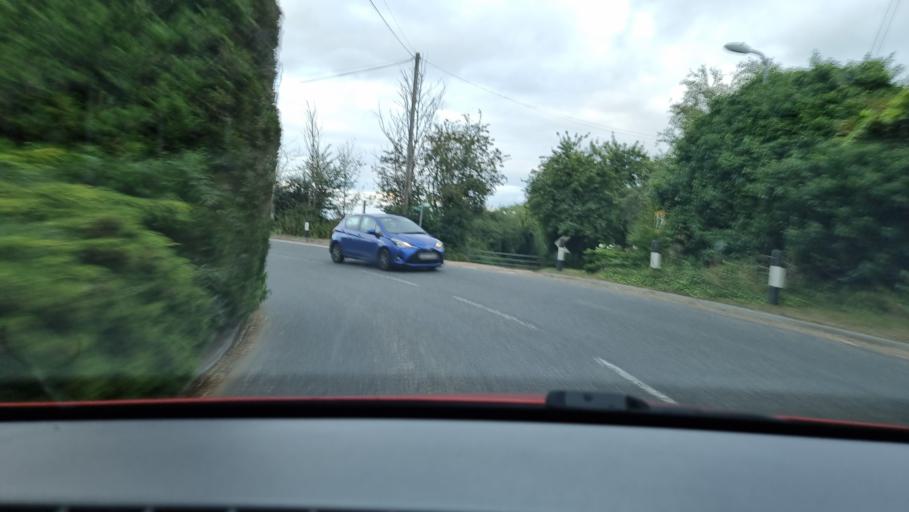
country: GB
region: England
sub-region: Buckinghamshire
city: Cheddington
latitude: 51.8656
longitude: -0.6567
